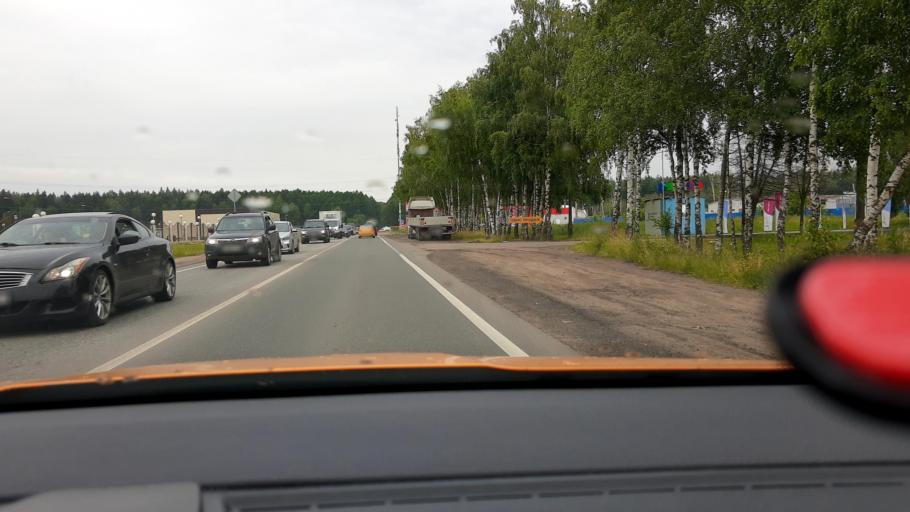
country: RU
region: Moskovskaya
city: Pirogovskiy
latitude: 55.9863
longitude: 37.7270
